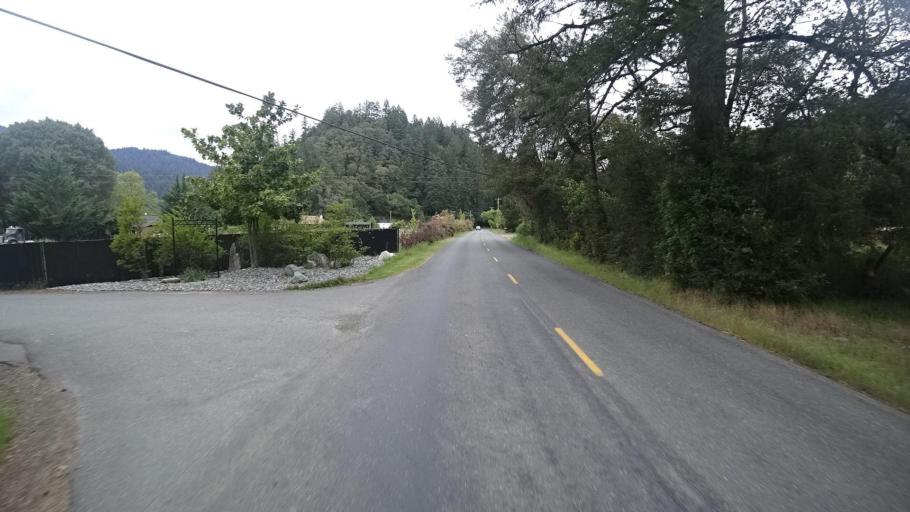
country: US
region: California
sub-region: Humboldt County
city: Willow Creek
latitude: 40.9488
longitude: -123.6306
